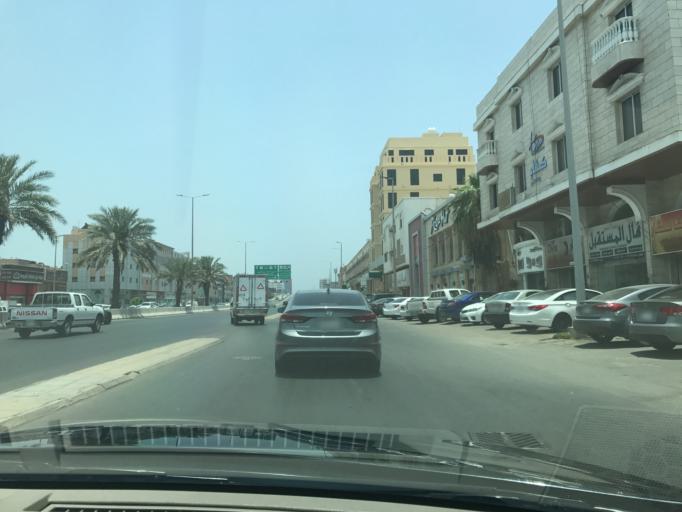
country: SA
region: Makkah
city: Jeddah
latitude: 21.5766
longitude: 39.1492
